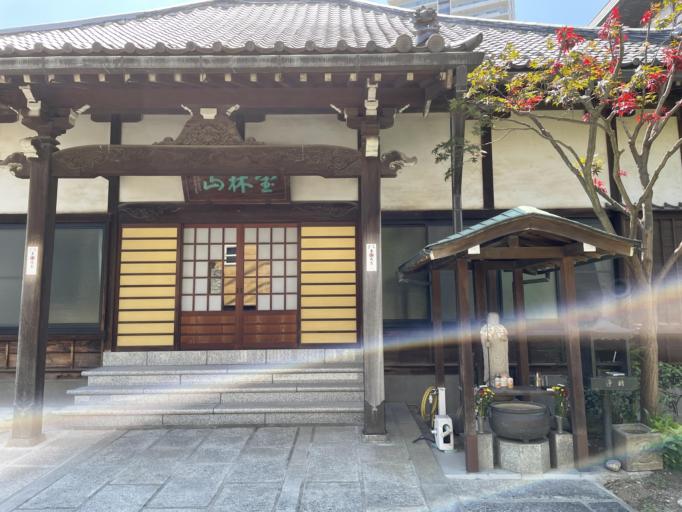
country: JP
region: Chiba
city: Matsudo
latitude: 35.7314
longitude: 139.8834
